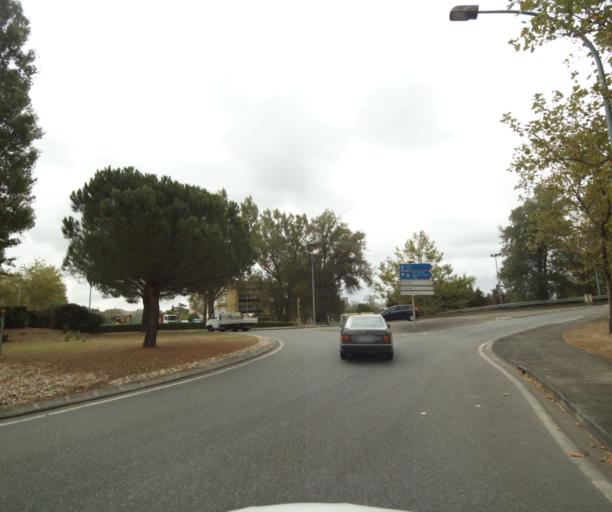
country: FR
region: Midi-Pyrenees
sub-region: Departement de la Haute-Garonne
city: Villefranche-de-Lauragais
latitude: 43.4061
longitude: 1.7088
